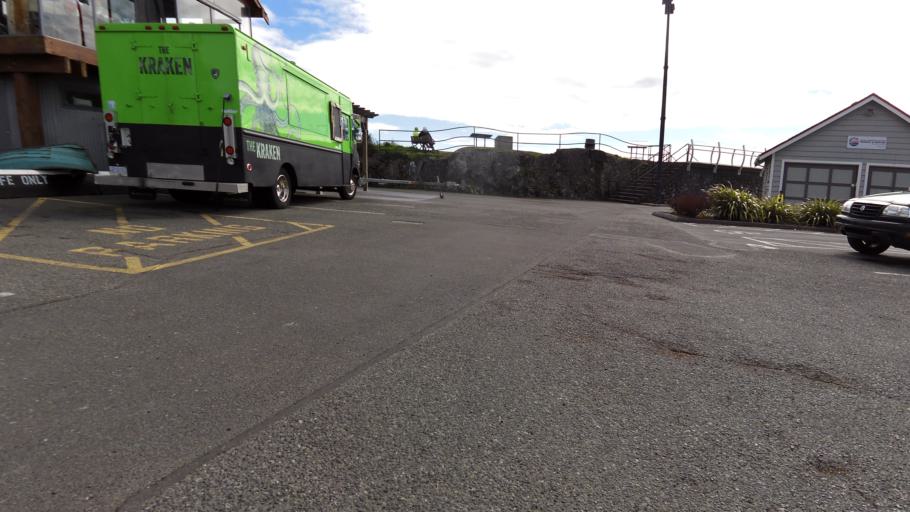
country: CA
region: British Columbia
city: Victoria
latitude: 48.4154
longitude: -123.3851
